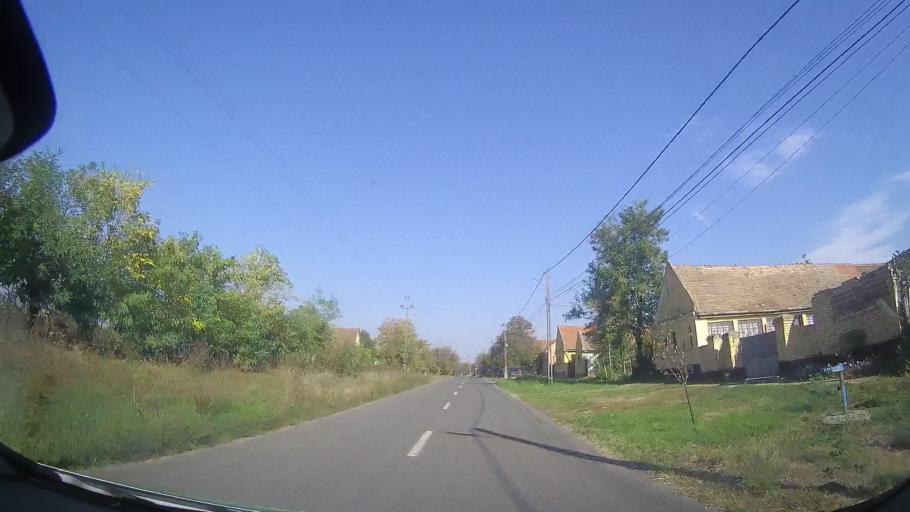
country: RO
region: Timis
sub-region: Comuna Topolovatu Mare
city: Topolovatu Mare
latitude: 45.8164
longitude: 21.5804
